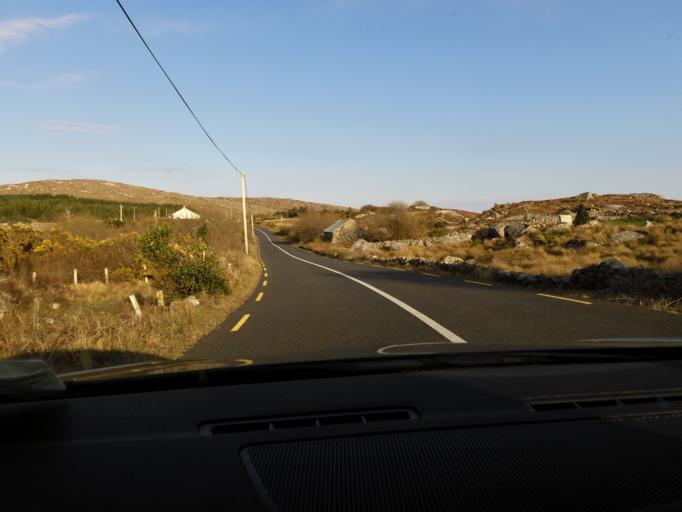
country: IE
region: Connaught
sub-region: County Galway
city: Oughterard
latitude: 53.3890
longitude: -9.6225
